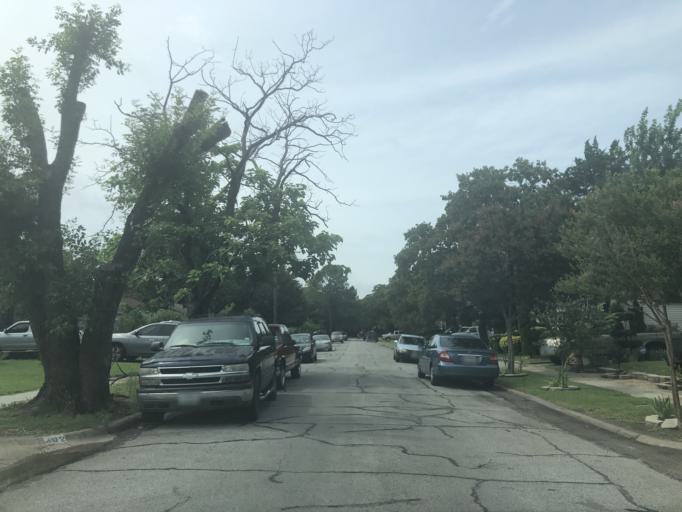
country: US
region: Texas
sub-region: Dallas County
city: Irving
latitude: 32.8113
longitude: -96.9693
